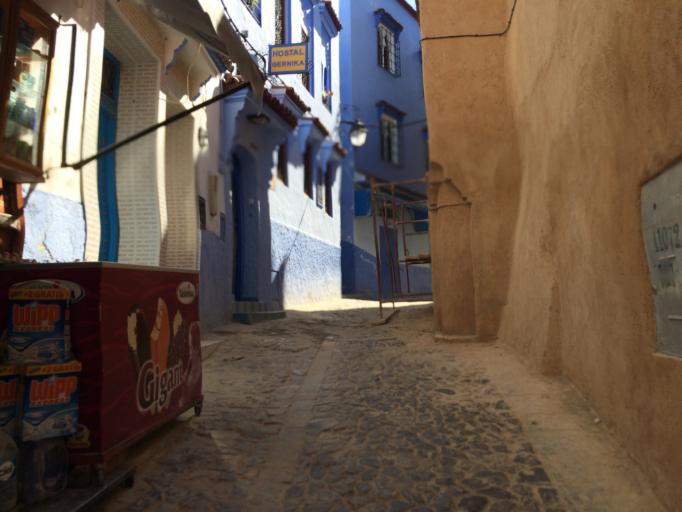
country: MA
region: Tanger-Tetouan
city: Chefchaouene
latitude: 35.1698
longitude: -5.2597
